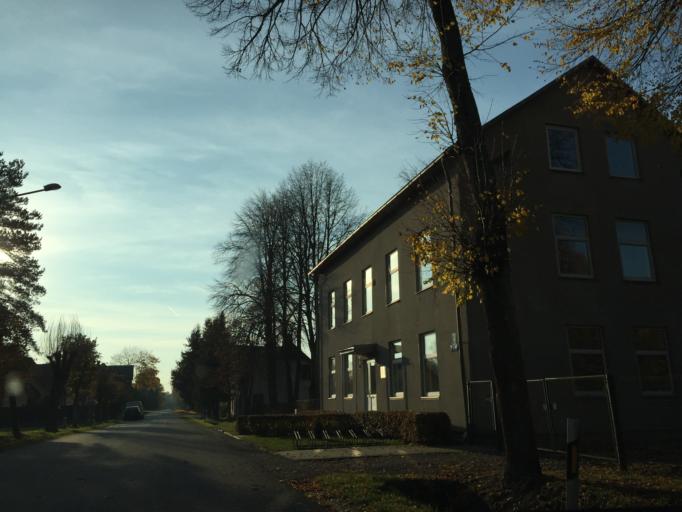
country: LV
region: Skrunda
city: Skrunda
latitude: 56.6766
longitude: 22.0123
